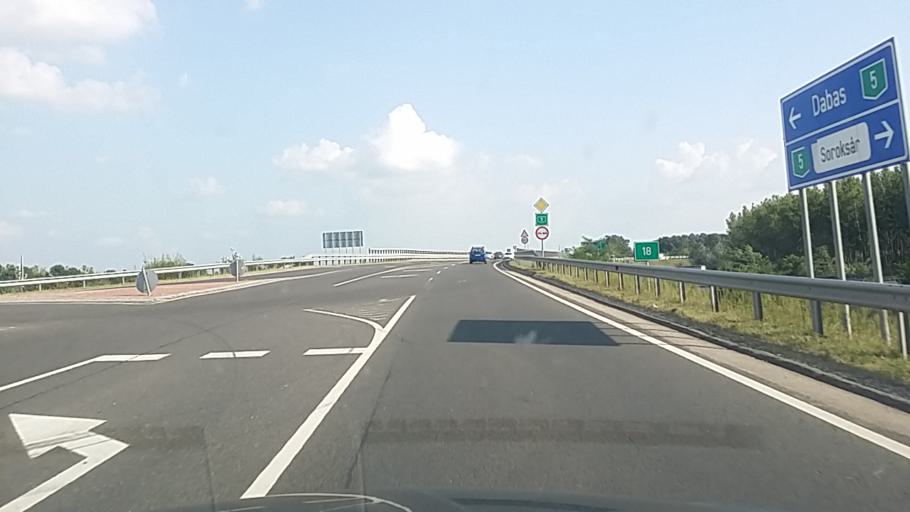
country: HU
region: Budapest
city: Budapest XXIII. keruelet
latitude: 47.3667
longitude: 19.1451
